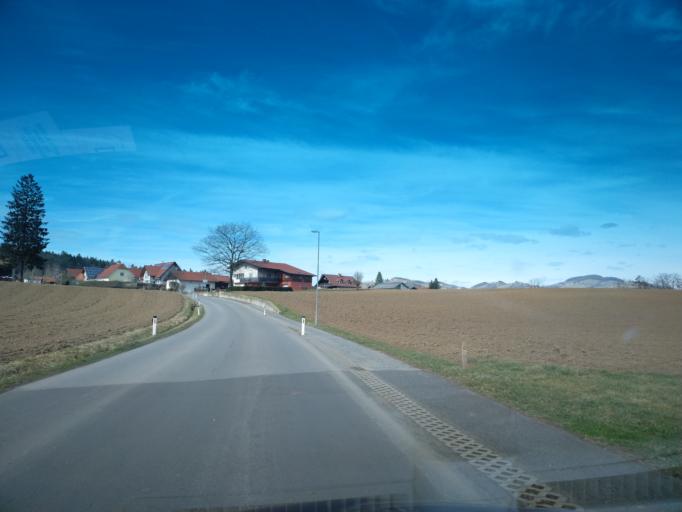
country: AT
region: Styria
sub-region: Politischer Bezirk Leibnitz
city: Grossklein
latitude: 46.7394
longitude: 15.4326
